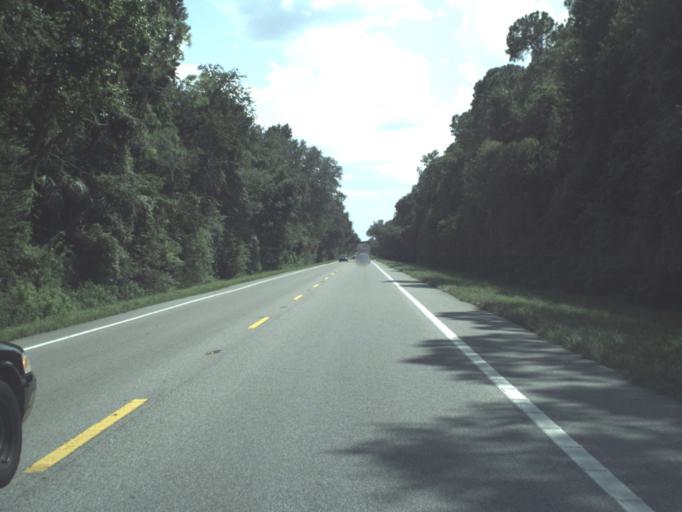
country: US
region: Florida
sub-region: Hillsborough County
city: Thonotosassa
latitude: 28.1214
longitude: -82.2395
